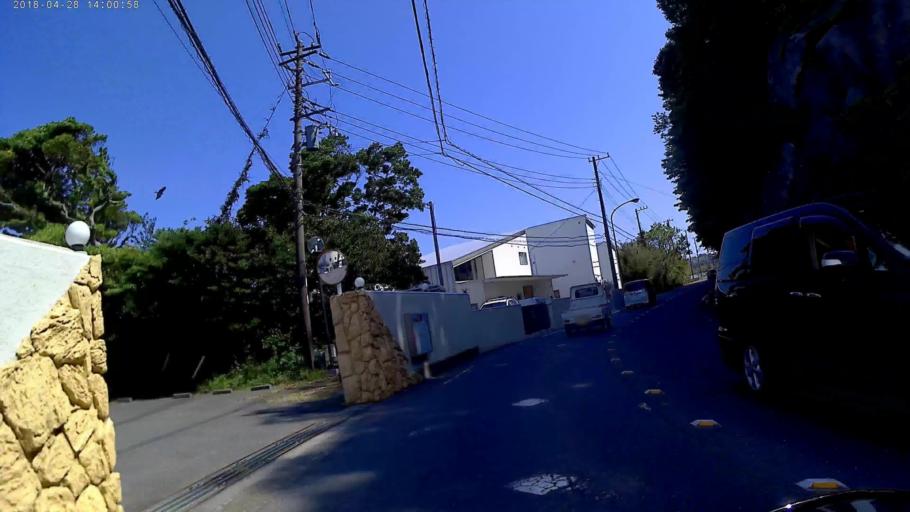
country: JP
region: Kanagawa
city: Miura
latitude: 35.1716
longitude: 139.6593
